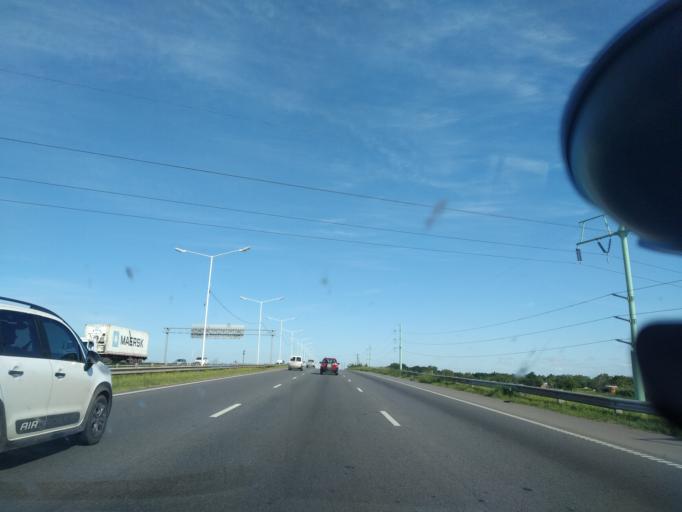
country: AR
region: Santa Fe
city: Gobernador Galvez
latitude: -32.9996
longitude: -60.6917
